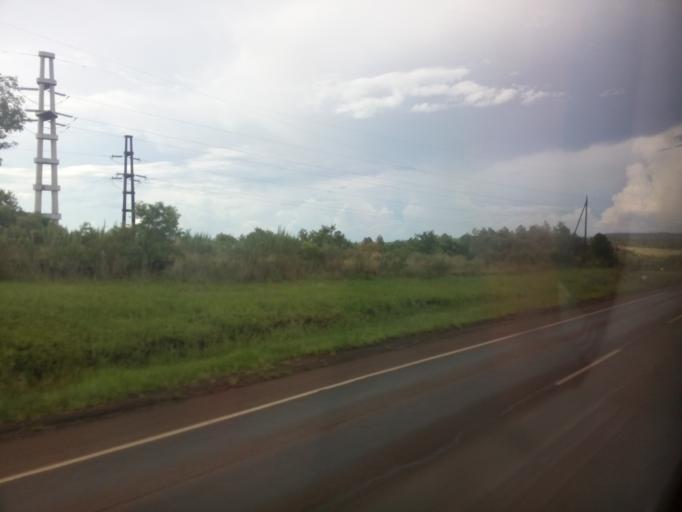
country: AR
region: Misiones
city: Santa Ana
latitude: -27.3958
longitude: -55.6007
